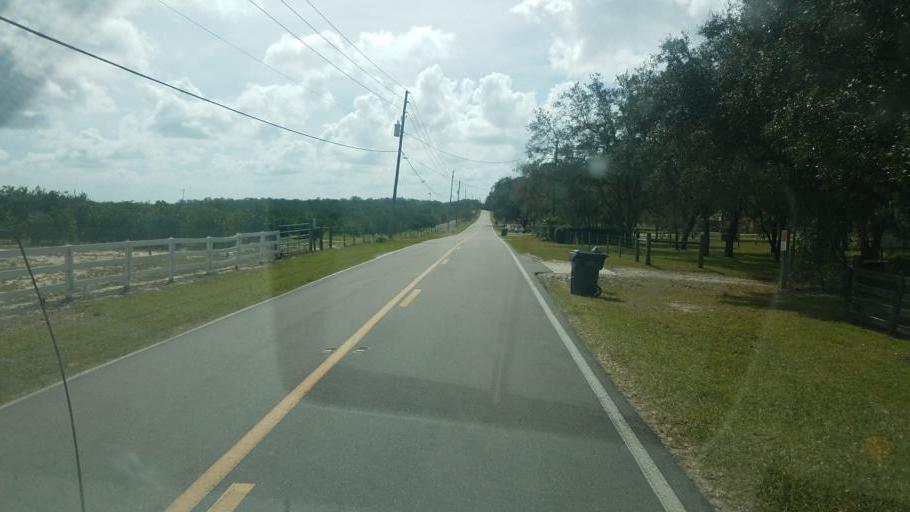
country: US
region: Florida
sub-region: Polk County
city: Dundee
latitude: 28.0487
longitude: -81.5333
